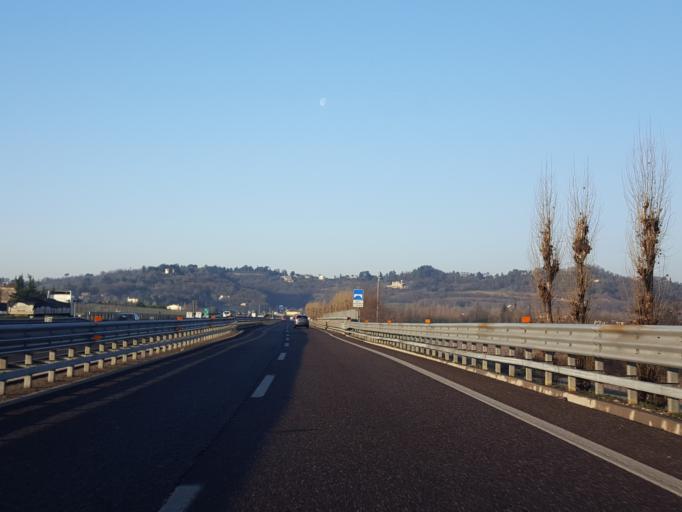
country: IT
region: Veneto
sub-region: Provincia di Vicenza
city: Arcugnano-Torri
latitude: 45.5175
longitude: 11.5796
